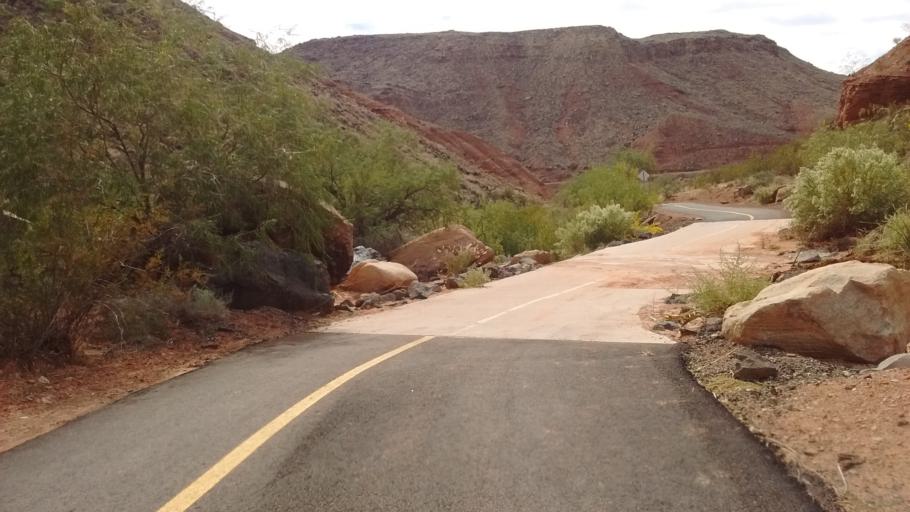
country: US
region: Utah
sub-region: Washington County
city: Washington
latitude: 37.1259
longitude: -113.4835
